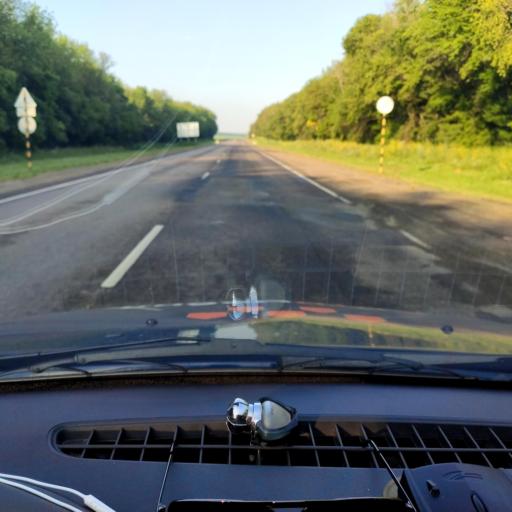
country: RU
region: Lipetsk
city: Izmalkovo
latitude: 52.4688
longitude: 38.0204
